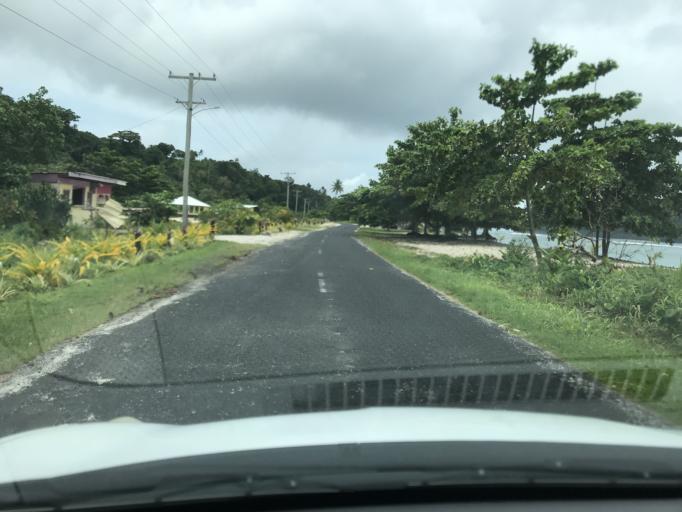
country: WS
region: Va`a-o-Fonoti
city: Samamea
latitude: -14.0455
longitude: -171.4510
